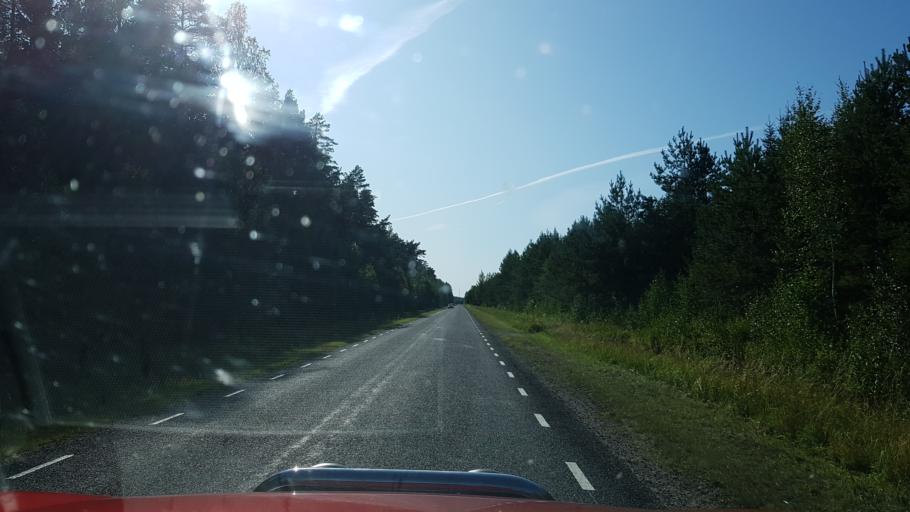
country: LV
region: Salacgrivas
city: Ainazi
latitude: 58.0811
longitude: 24.5543
